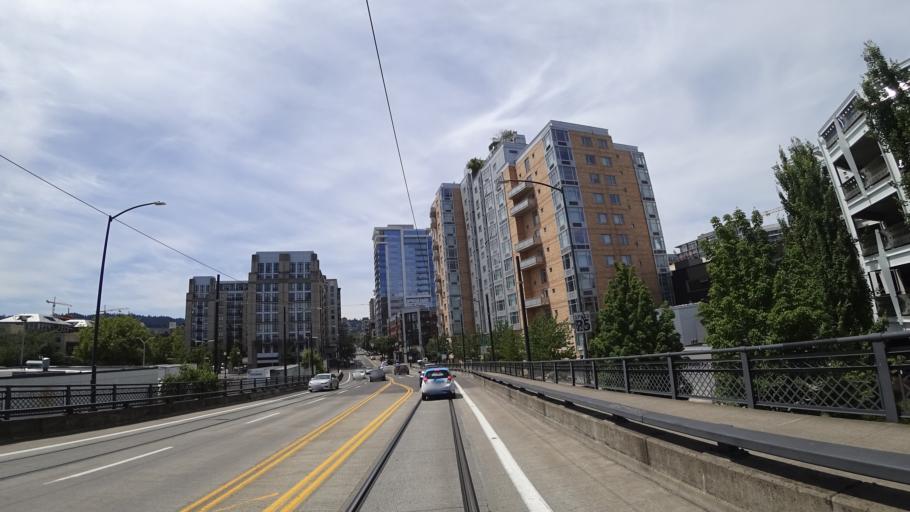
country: US
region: Oregon
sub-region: Multnomah County
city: Portland
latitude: 45.5301
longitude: -122.6790
